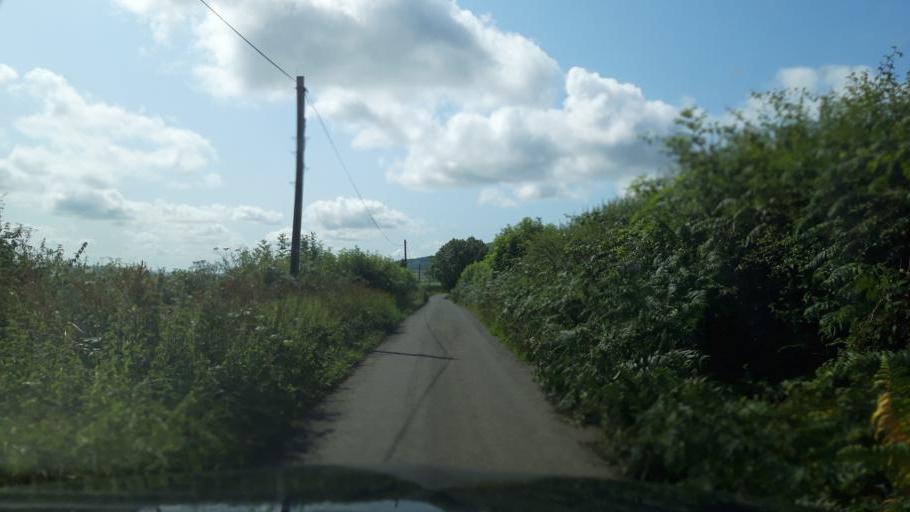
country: IE
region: Leinster
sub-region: Kilkenny
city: Graiguenamanagh
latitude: 52.5644
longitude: -6.9801
